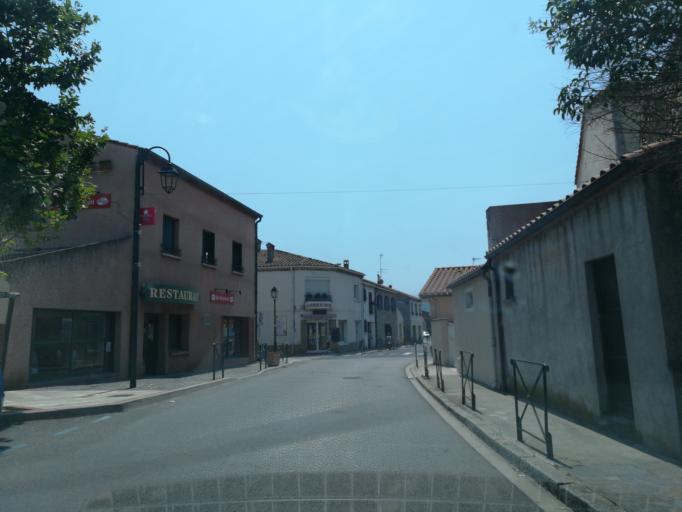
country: FR
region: Languedoc-Roussillon
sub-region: Departement des Pyrenees-Orientales
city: Sant Joan de Pladecorts
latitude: 42.5111
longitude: 2.7907
